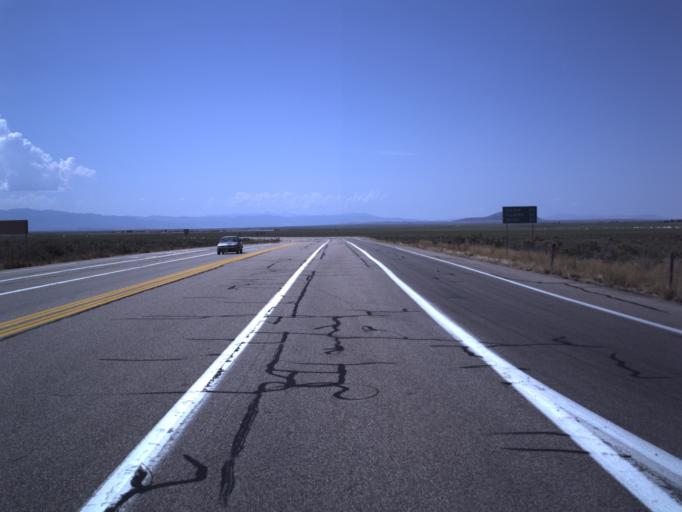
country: US
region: Utah
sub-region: Millard County
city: Delta
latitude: 39.3529
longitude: -112.4966
